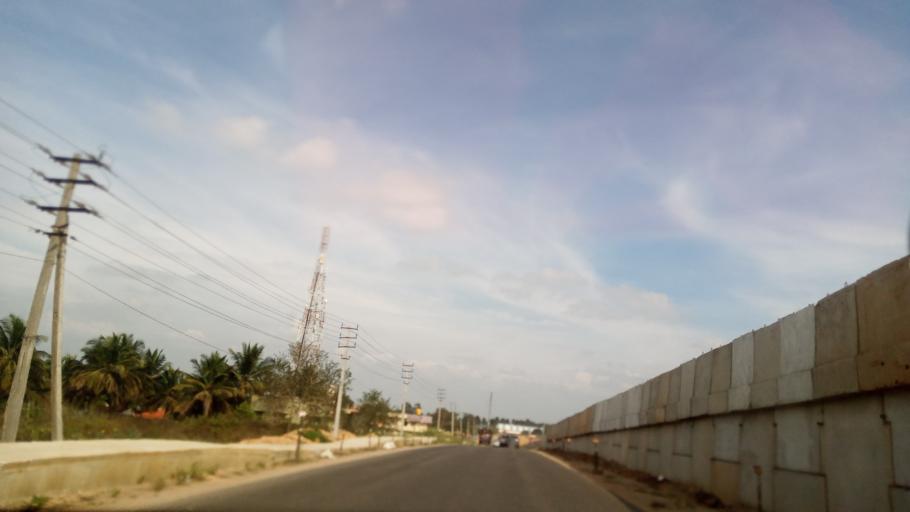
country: IN
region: Karnataka
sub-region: Mandya
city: Mandya
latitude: 12.4965
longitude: 76.8054
